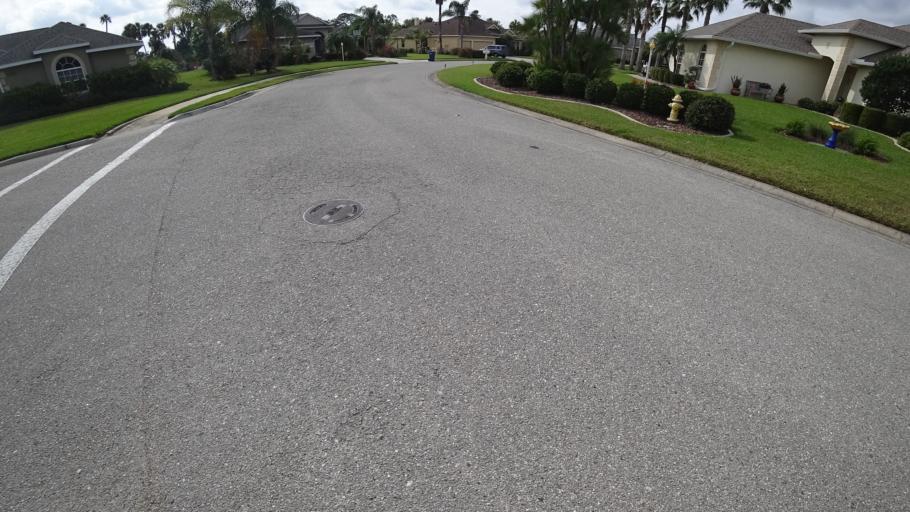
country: US
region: Florida
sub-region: Manatee County
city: Ellenton
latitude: 27.5703
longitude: -82.4720
